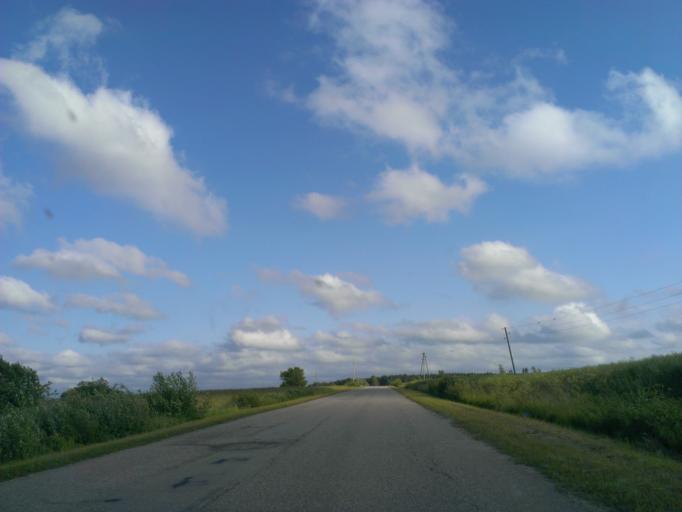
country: LV
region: Aizpute
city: Aizpute
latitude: 56.7808
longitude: 21.5178
